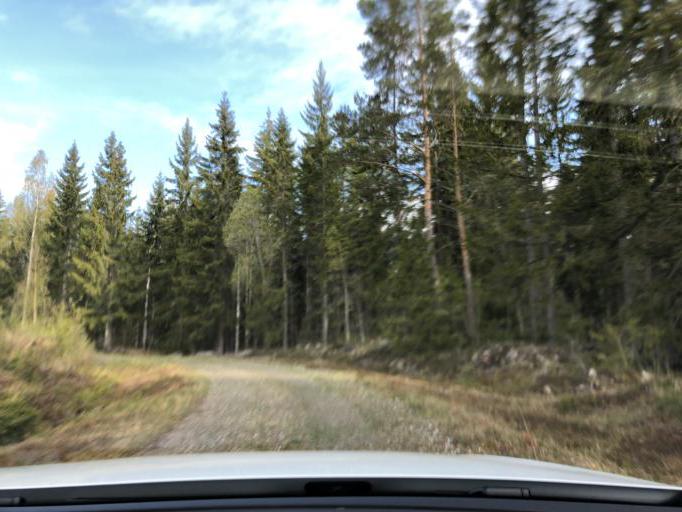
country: SE
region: Uppsala
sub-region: Heby Kommun
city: Tarnsjo
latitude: 60.2943
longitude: 16.8236
